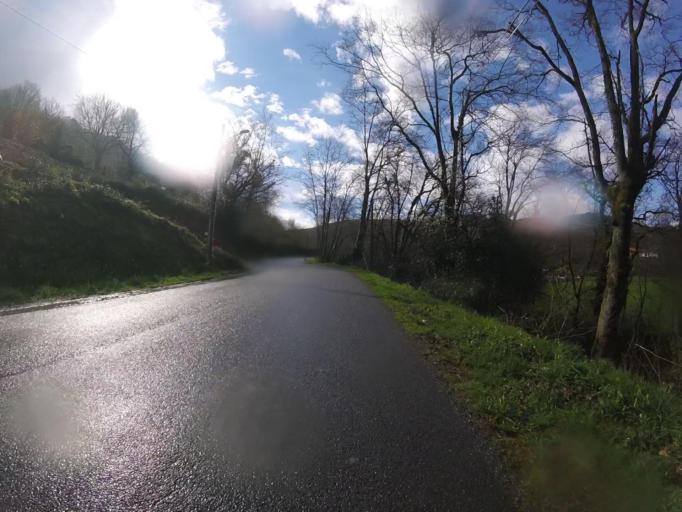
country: FR
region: Aquitaine
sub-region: Departement des Pyrenees-Atlantiques
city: Ascain
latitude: 43.3425
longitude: -1.6163
